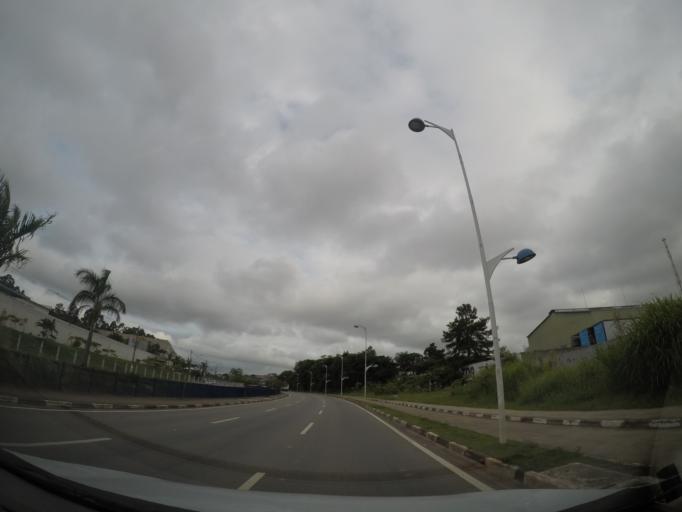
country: BR
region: Sao Paulo
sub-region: Aruja
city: Aruja
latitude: -23.4021
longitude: -46.3507
